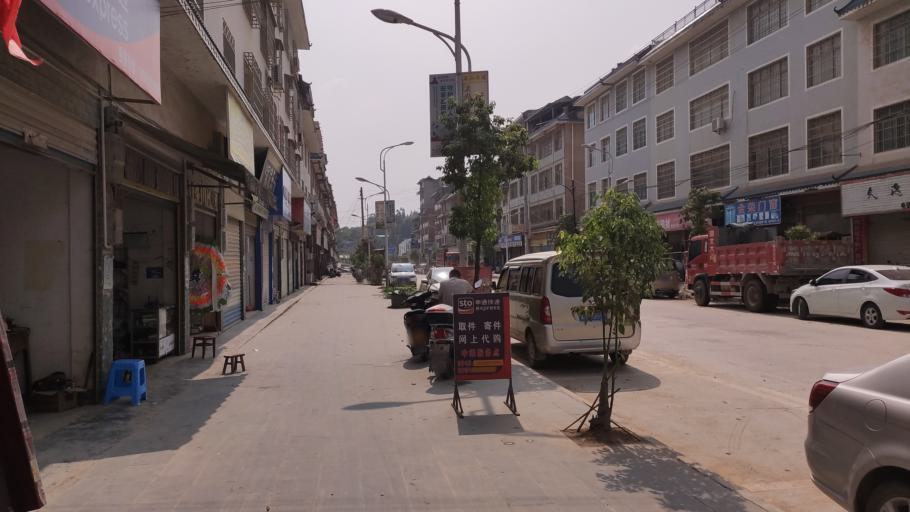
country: CN
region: Guizhou Sheng
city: Zhongchao
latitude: 26.1366
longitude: 109.2162
